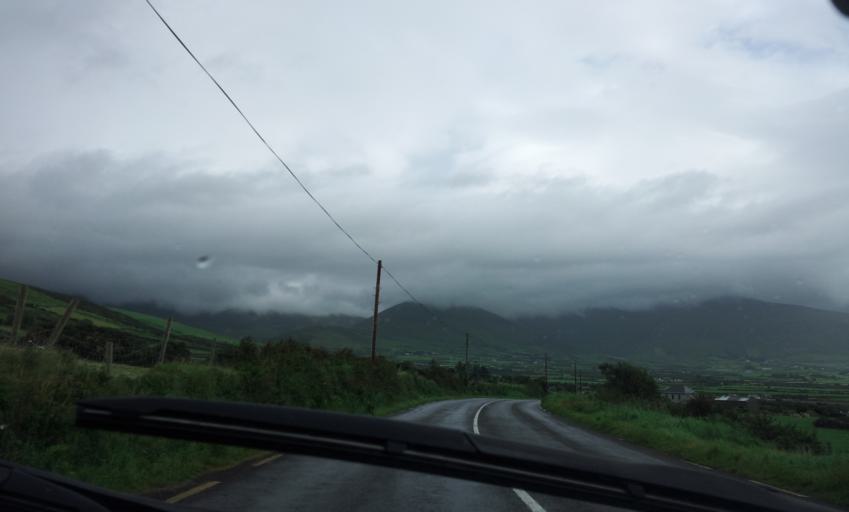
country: IE
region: Munster
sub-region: Ciarrai
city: Dingle
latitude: 52.1333
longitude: -10.2436
